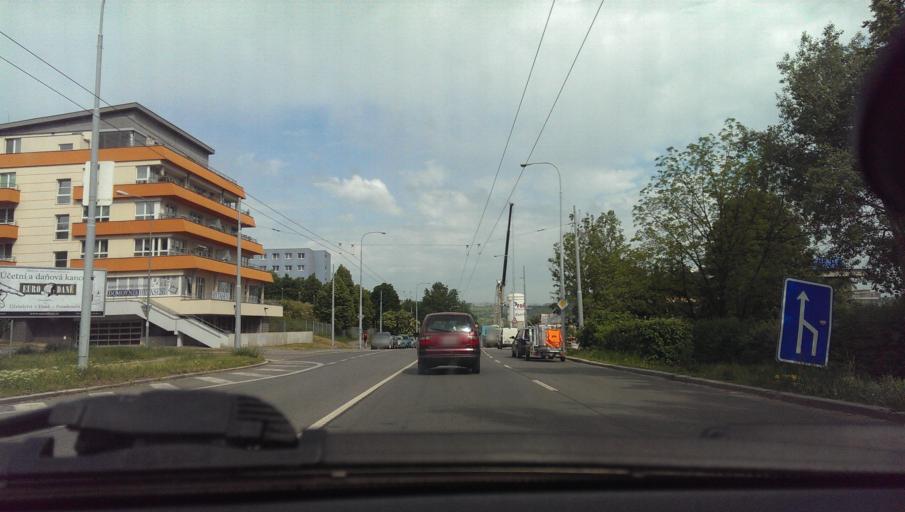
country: CZ
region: South Moravian
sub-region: Mesto Brno
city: Brno
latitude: 49.2149
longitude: 16.6285
